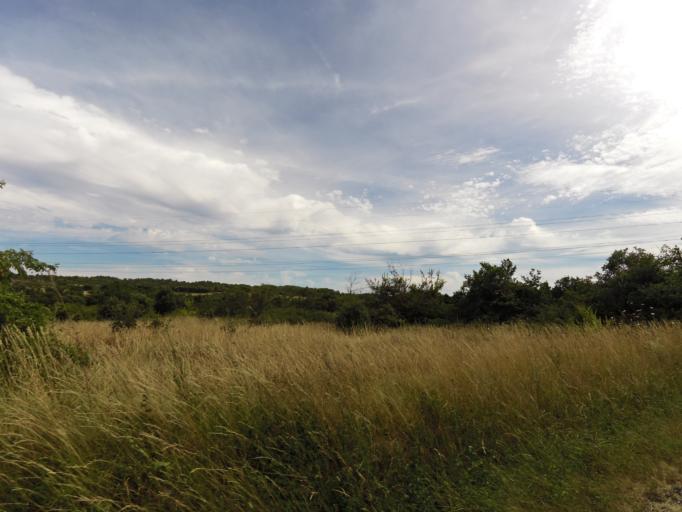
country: FR
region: Languedoc-Roussillon
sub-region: Departement du Gard
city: Saint-Mamert-du-Gard
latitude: 43.8767
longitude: 4.1774
